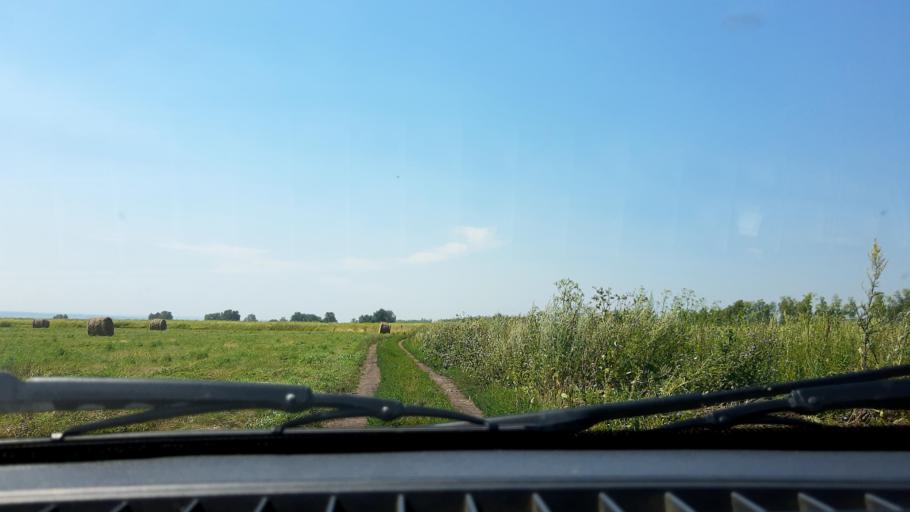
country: RU
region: Bashkortostan
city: Kushnarenkovo
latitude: 55.0760
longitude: 55.1692
